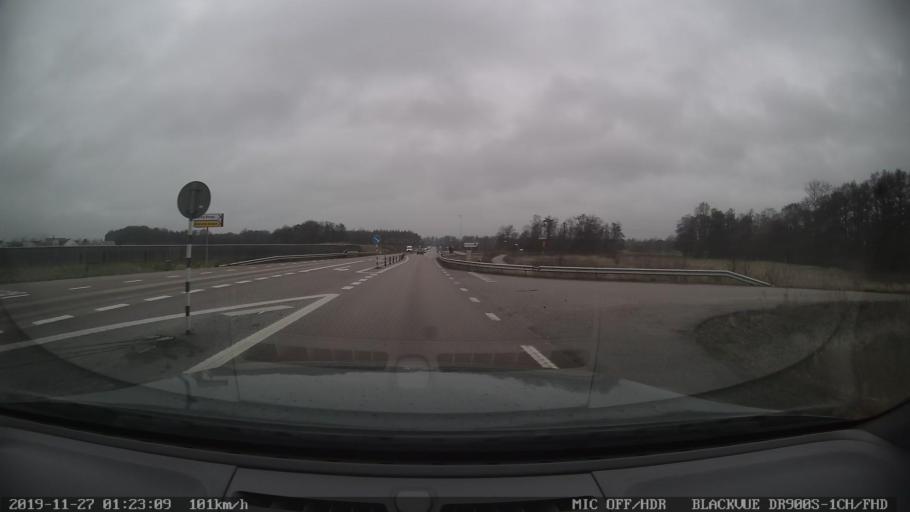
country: SE
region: Skane
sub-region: Helsingborg
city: Helsingborg
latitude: 56.0997
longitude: 12.6673
